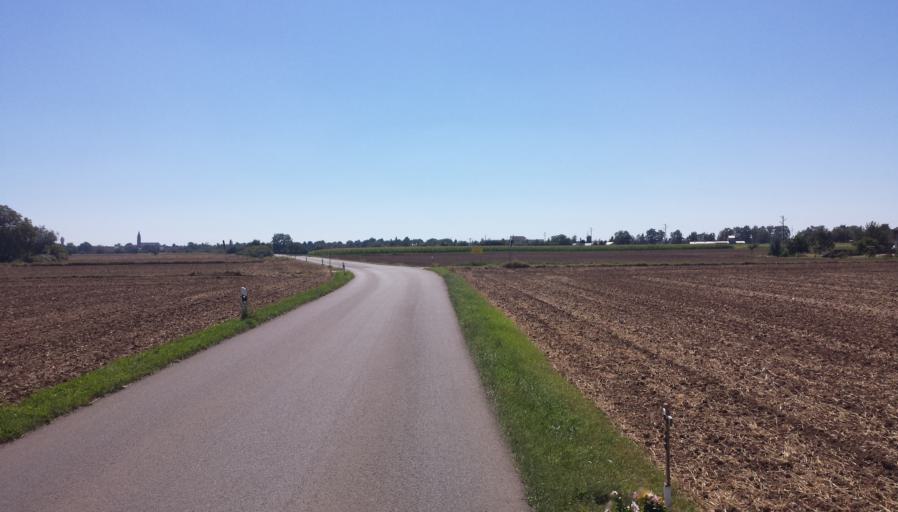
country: DE
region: Baden-Wuerttemberg
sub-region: Karlsruhe Region
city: Plankstadt
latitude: 49.4111
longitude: 8.5928
